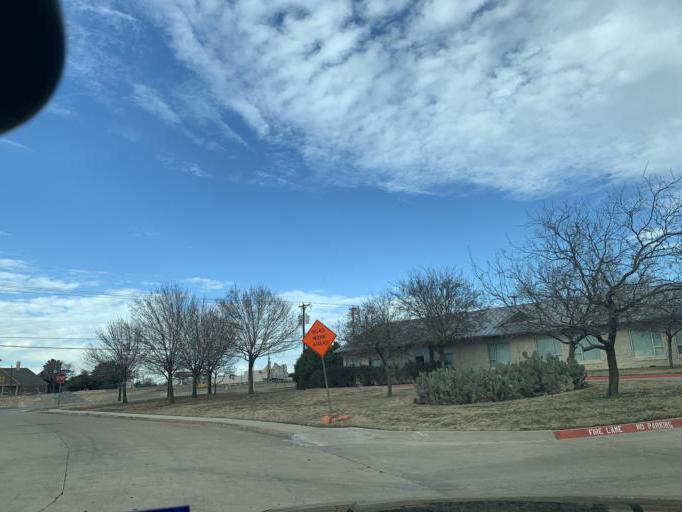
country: US
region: Texas
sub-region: Dallas County
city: Duncanville
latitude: 32.6307
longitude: -96.9008
